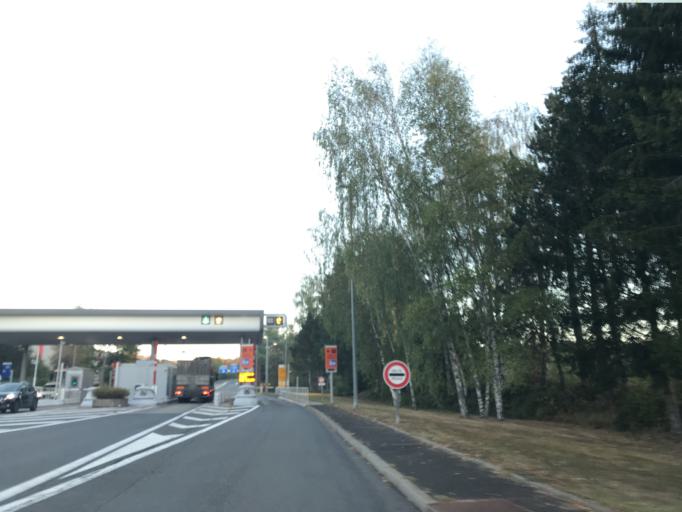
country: FR
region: Auvergne
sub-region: Departement du Puy-de-Dome
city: Celles-sur-Durolle
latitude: 45.8784
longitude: 3.6255
